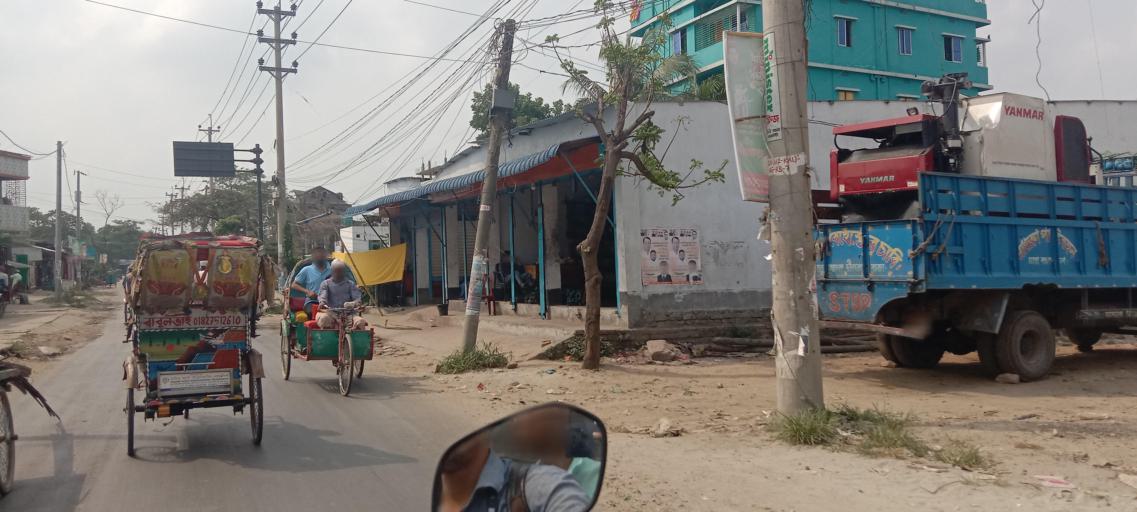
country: BD
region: Dhaka
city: Azimpur
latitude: 23.7152
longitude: 90.3554
